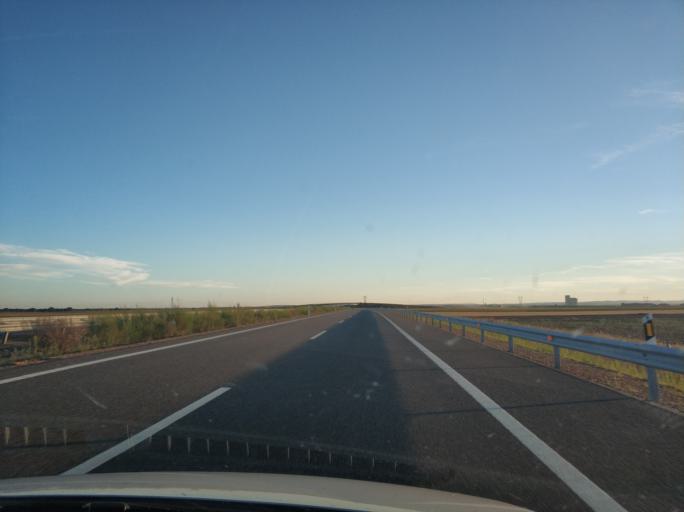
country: ES
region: Castille and Leon
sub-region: Provincia de Zamora
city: Barcial del Barco
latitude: 41.9450
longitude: -5.6339
